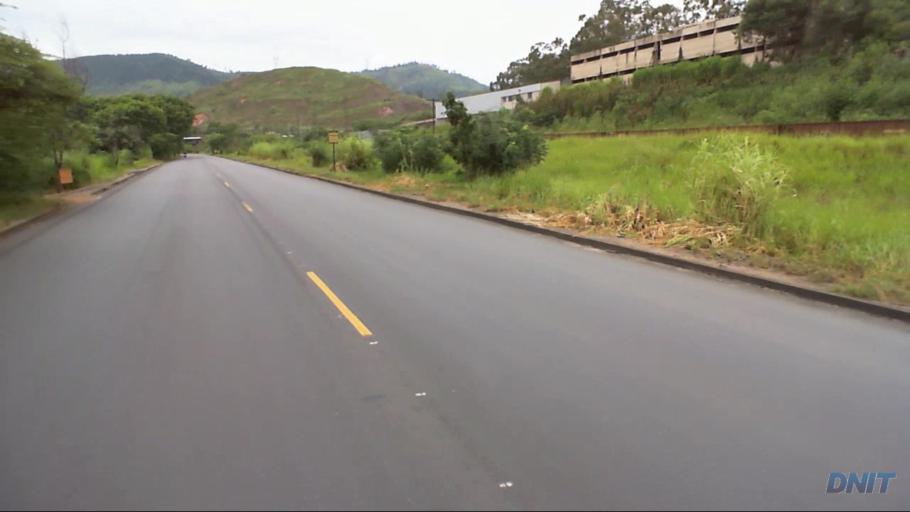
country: BR
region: Minas Gerais
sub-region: Coronel Fabriciano
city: Coronel Fabriciano
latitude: -19.5301
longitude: -42.6316
